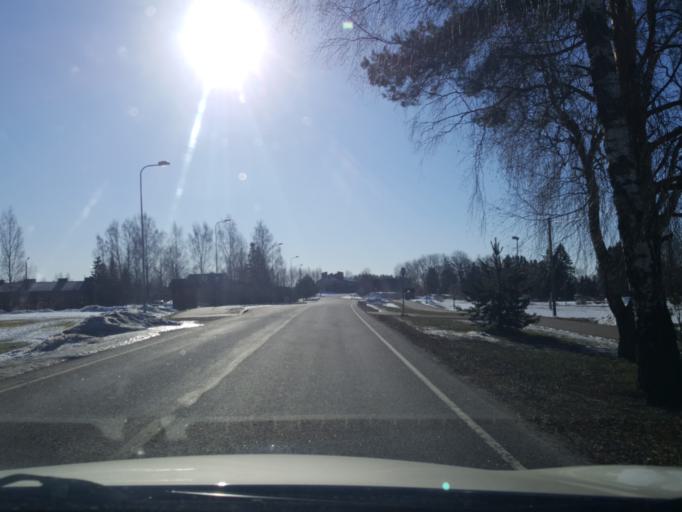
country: EE
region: Viljandimaa
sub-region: Viiratsi vald
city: Viiratsi
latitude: 58.4305
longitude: 25.6839
